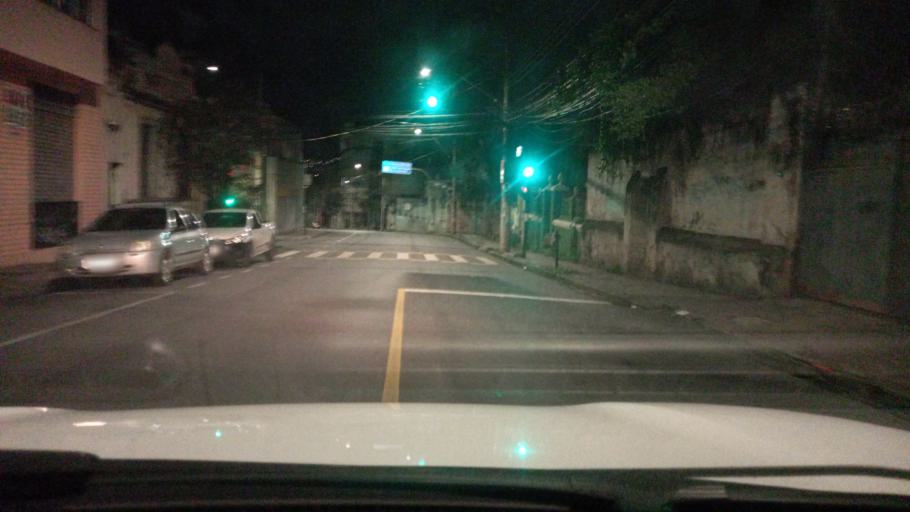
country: BR
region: Minas Gerais
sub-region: Belo Horizonte
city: Belo Horizonte
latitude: -19.9080
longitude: -43.9448
